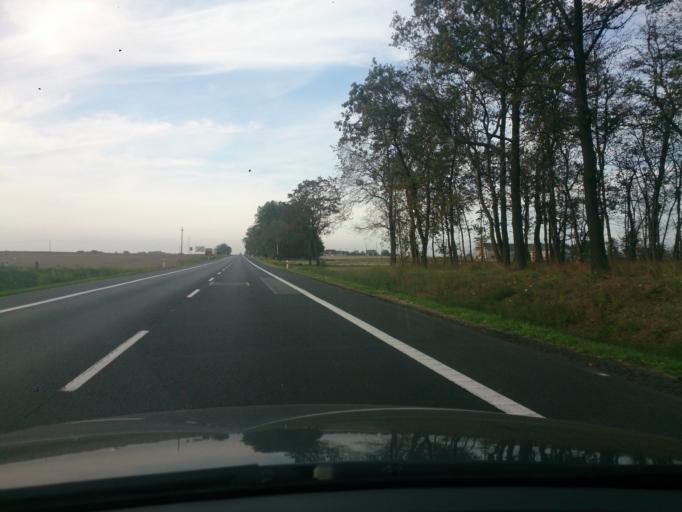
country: PL
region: Kujawsko-Pomorskie
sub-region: Powiat swiecki
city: Bukowiec
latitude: 53.3652
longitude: 18.3190
